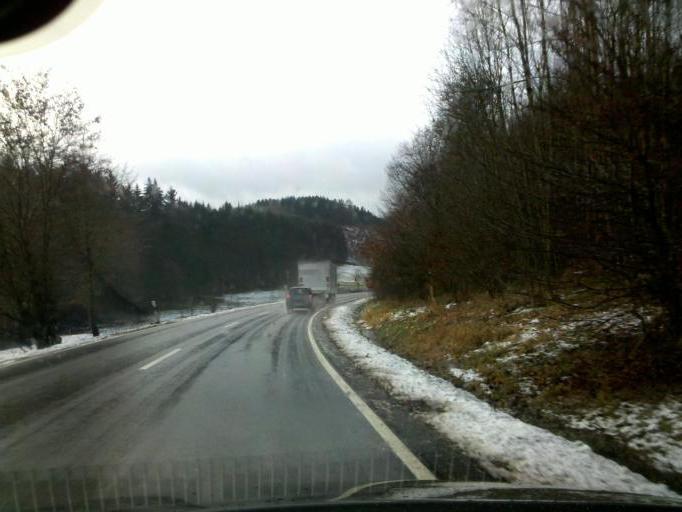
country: DE
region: Hesse
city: Dillenburg
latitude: 50.8353
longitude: 8.3503
